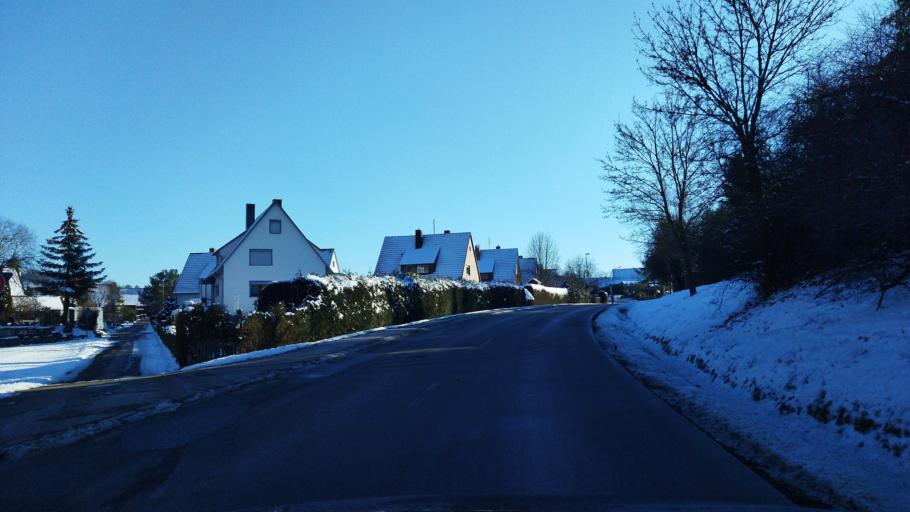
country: DE
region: Baden-Wuerttemberg
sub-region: Regierungsbezirk Stuttgart
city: Buhlertann
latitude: 49.0442
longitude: 9.9045
